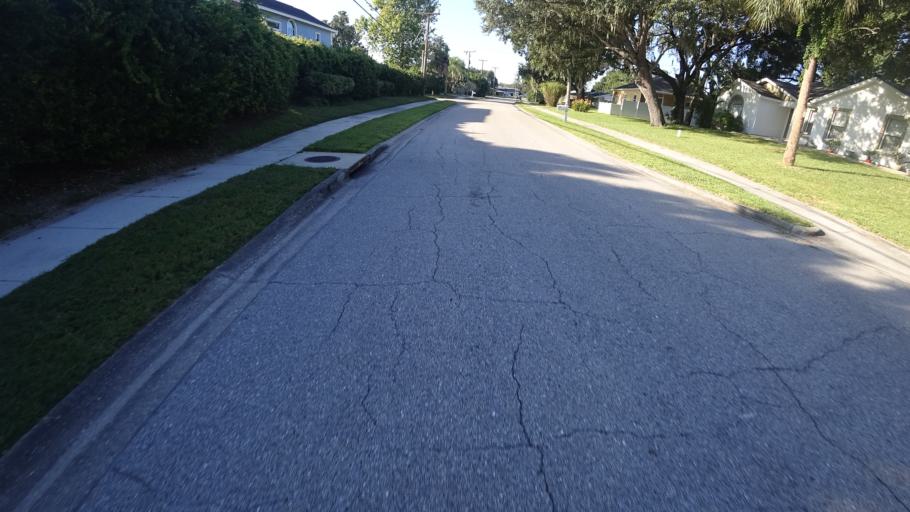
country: US
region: Florida
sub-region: Manatee County
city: Ellenton
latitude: 27.5018
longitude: -82.5091
